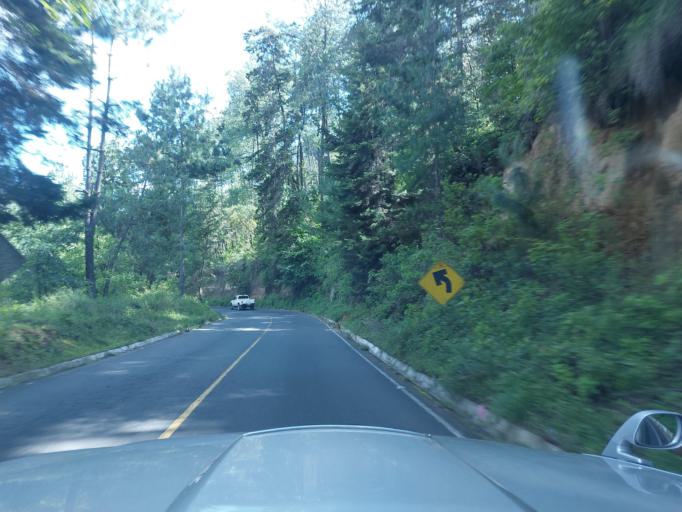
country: GT
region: Chimaltenango
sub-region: Municipio de Santa Cruz Balanya
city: Santa Cruz Balanya
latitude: 14.6875
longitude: -90.8960
